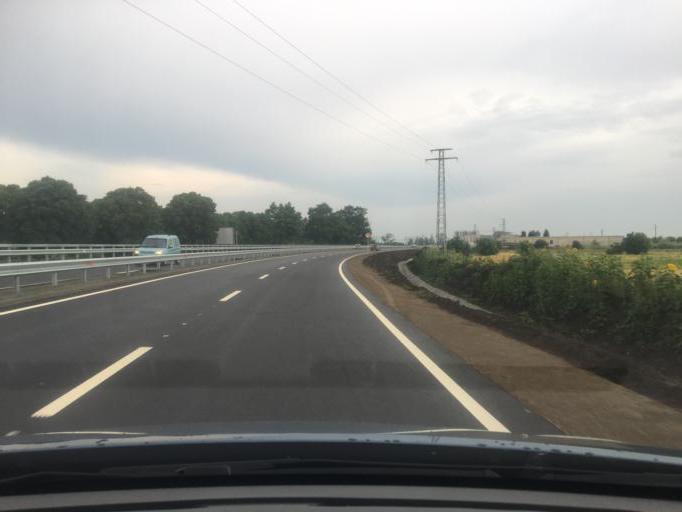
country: BG
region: Burgas
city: Aheloy
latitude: 42.6396
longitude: 27.6390
